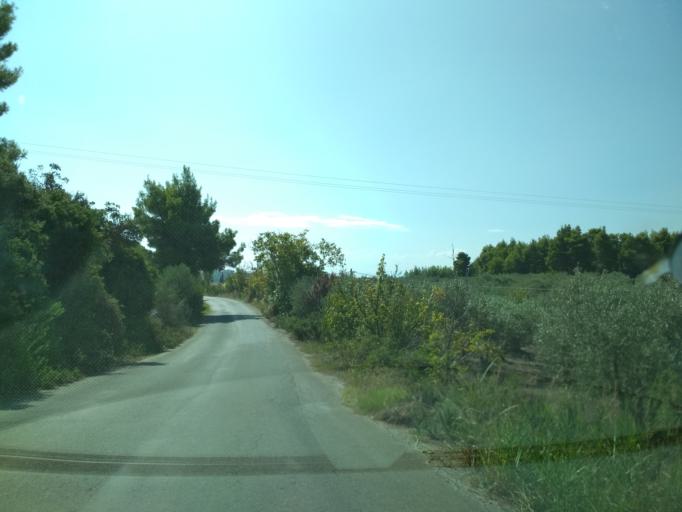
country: GR
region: Central Greece
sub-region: Nomos Evvoias
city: Roviai
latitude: 38.8245
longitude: 23.2457
